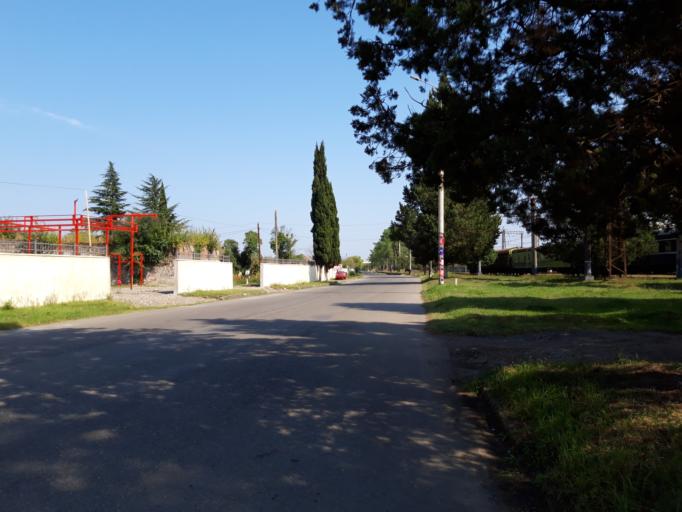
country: GE
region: Imereti
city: Samtredia
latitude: 42.1627
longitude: 42.3490
